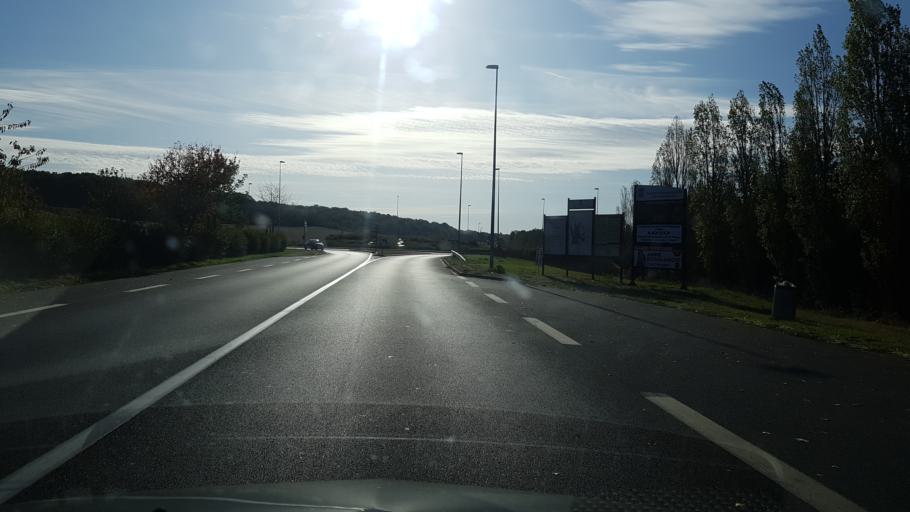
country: FR
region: Centre
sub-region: Departement du Loiret
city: Saint-Brisson-sur-Loire
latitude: 47.6597
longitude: 2.7119
